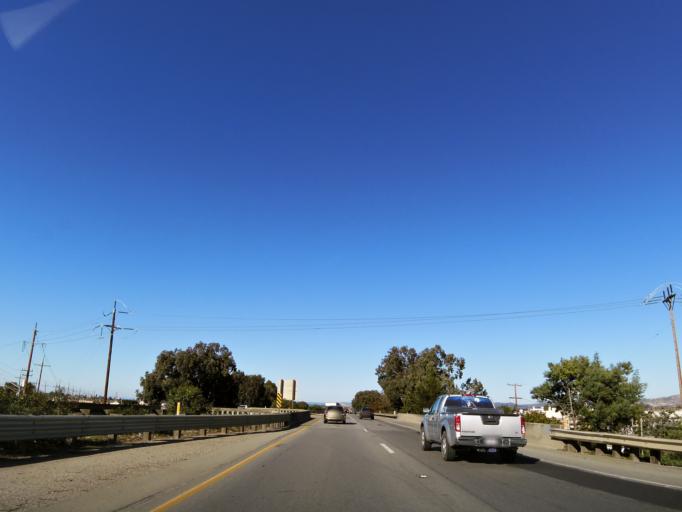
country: US
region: California
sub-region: Monterey County
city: Salinas
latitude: 36.6737
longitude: -121.6406
